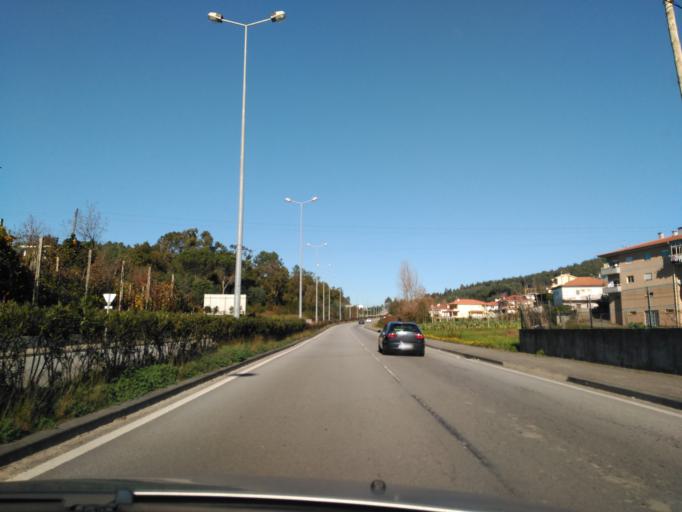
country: PT
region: Braga
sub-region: Braga
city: Adaufe
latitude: 41.5742
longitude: -8.3690
